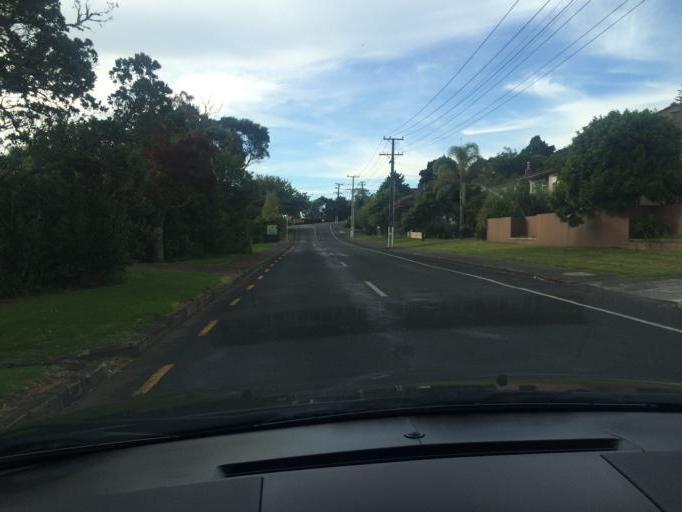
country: NZ
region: Auckland
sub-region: Auckland
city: Auckland
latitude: -36.8656
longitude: 174.7962
